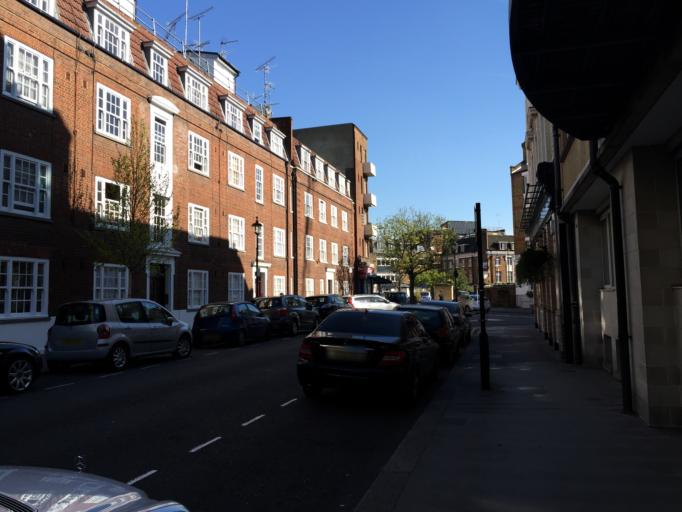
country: GB
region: England
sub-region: Greater London
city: London
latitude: 51.4940
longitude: -0.1329
